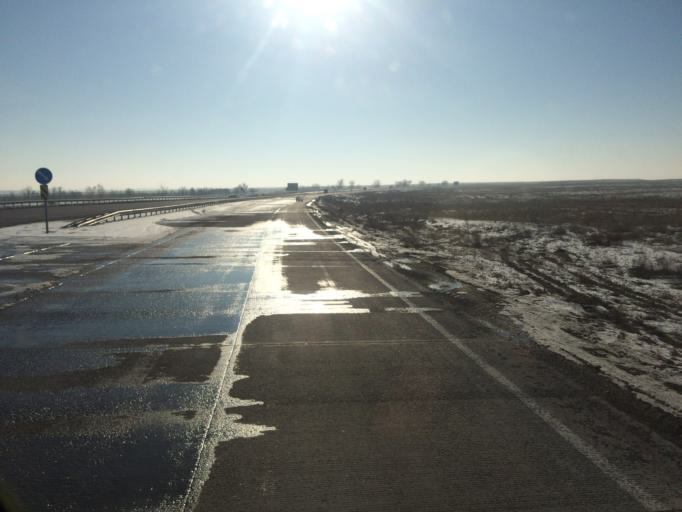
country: KG
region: Chuy
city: Kara-Balta
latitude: 43.1860
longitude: 73.9411
